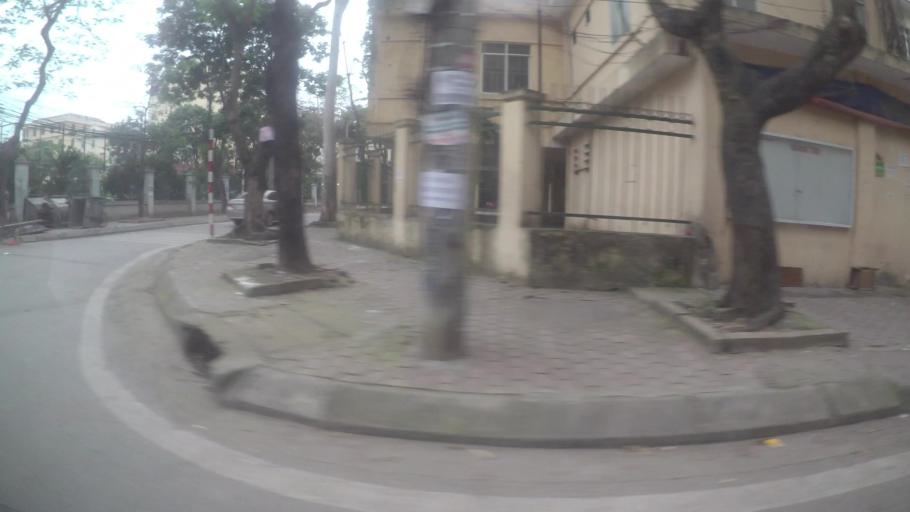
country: VN
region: Ha Noi
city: Cau Dien
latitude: 21.0373
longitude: 105.7658
